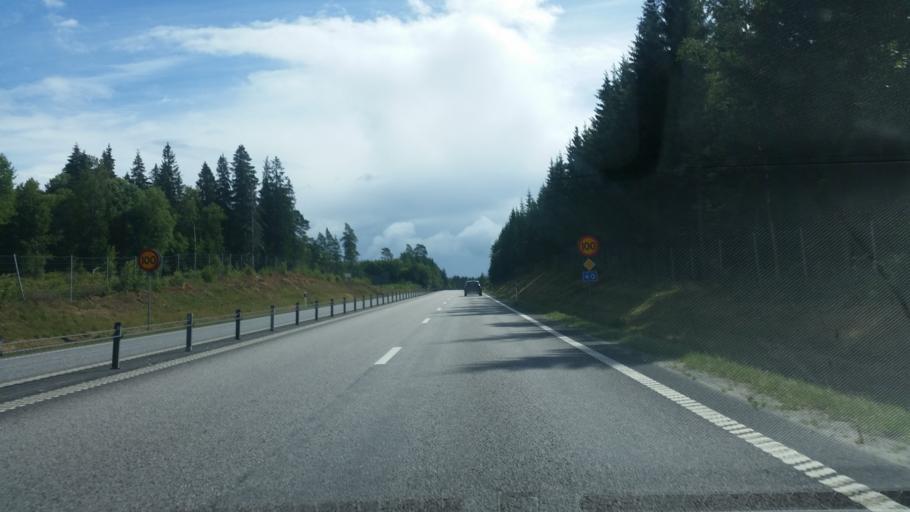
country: SE
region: Joenkoeping
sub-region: Mullsjo Kommun
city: Mullsjoe
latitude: 57.7748
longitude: 13.6878
